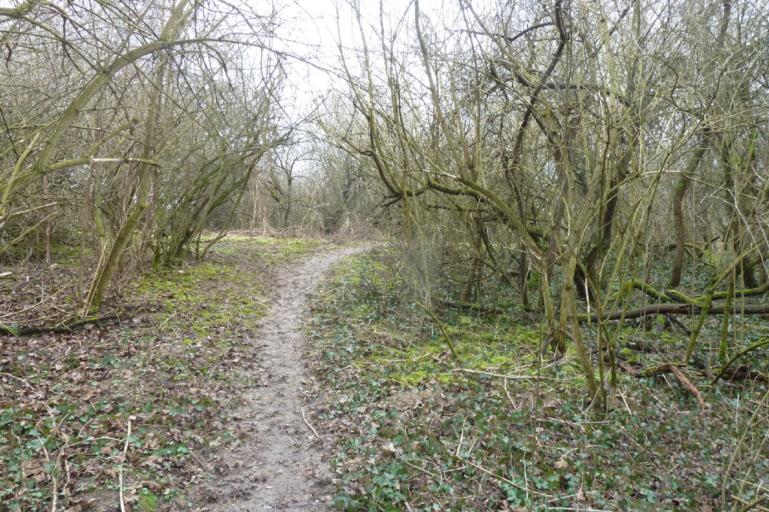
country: HU
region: Pest
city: Vacszentlaszlo
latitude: 47.6017
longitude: 19.5228
